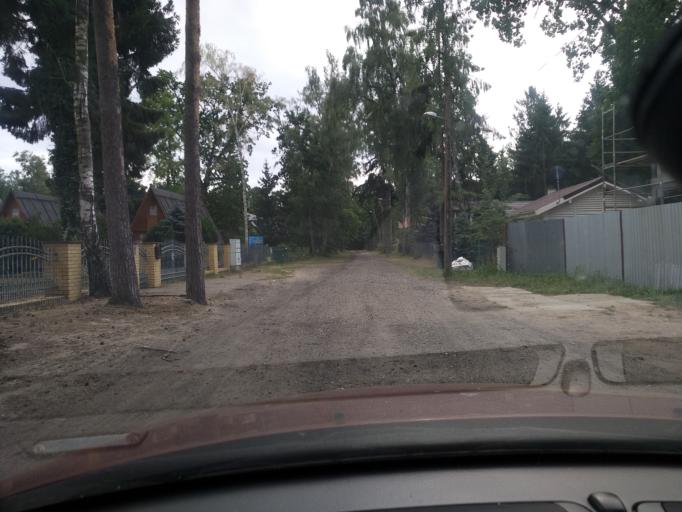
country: PL
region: West Pomeranian Voivodeship
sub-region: Powiat gryficki
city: Pobierowo
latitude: 54.0547
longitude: 14.9247
